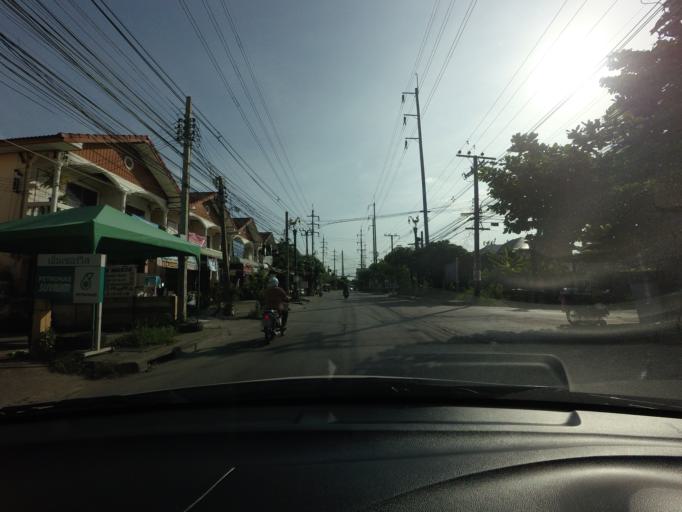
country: TH
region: Samut Prakan
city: Phra Pradaeng
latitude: 13.6668
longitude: 100.5495
